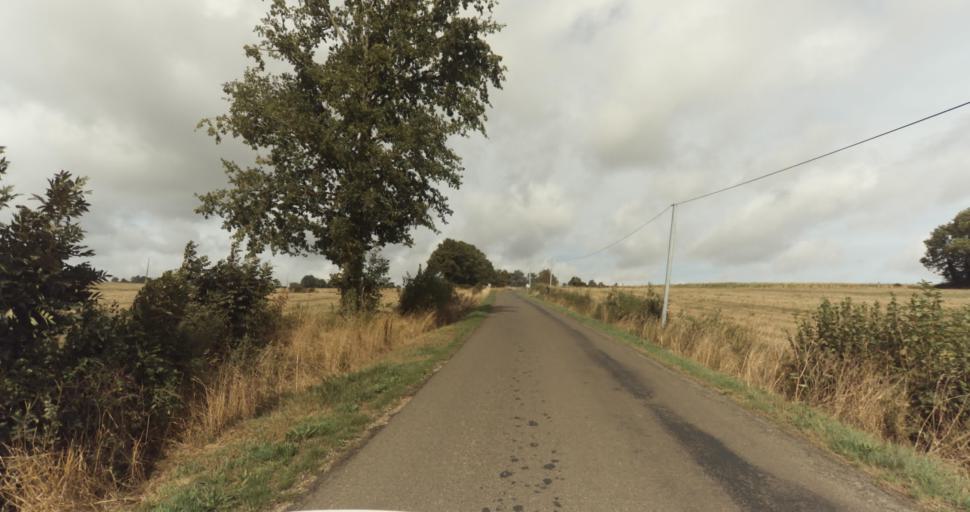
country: FR
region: Lower Normandy
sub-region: Departement de l'Orne
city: Gace
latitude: 48.8385
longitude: 0.3790
